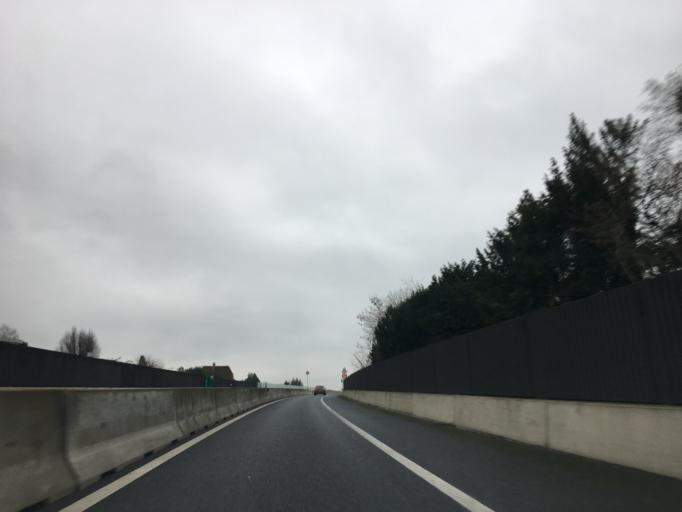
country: CH
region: Neuchatel
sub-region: Neuchatel District
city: Le Landeron
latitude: 47.0598
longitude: 7.0762
